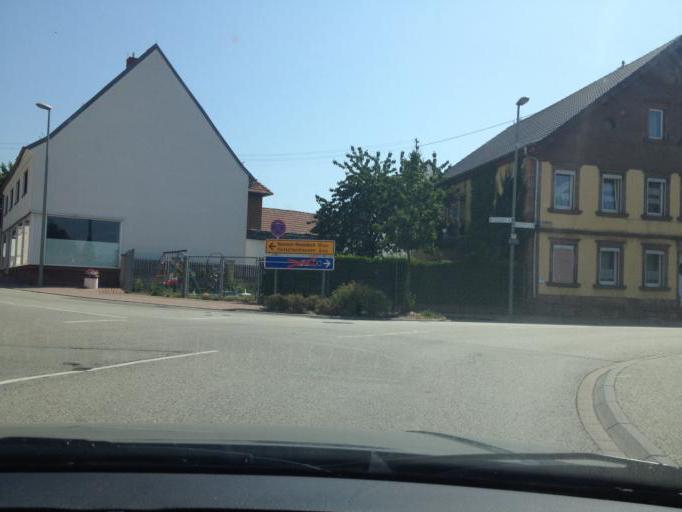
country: DE
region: Rheinland-Pfalz
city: Bruchmuhlbach-Miesau
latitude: 49.4048
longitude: 7.4376
